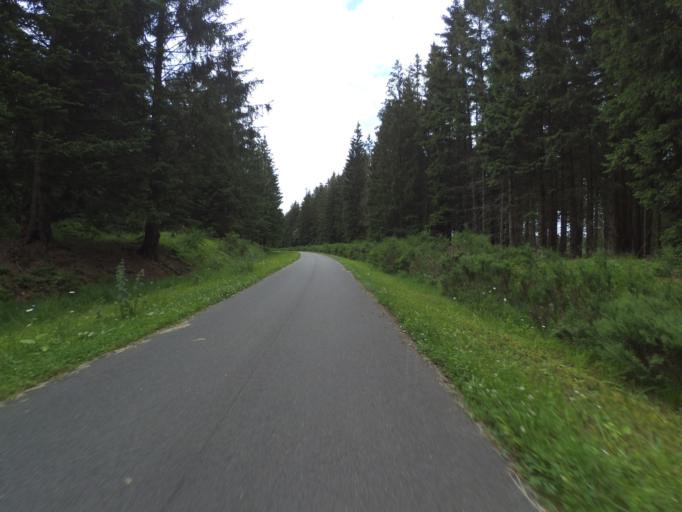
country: DE
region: North Rhine-Westphalia
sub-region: Regierungsbezirk Koln
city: Roetgen
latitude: 50.6432
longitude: 6.2409
